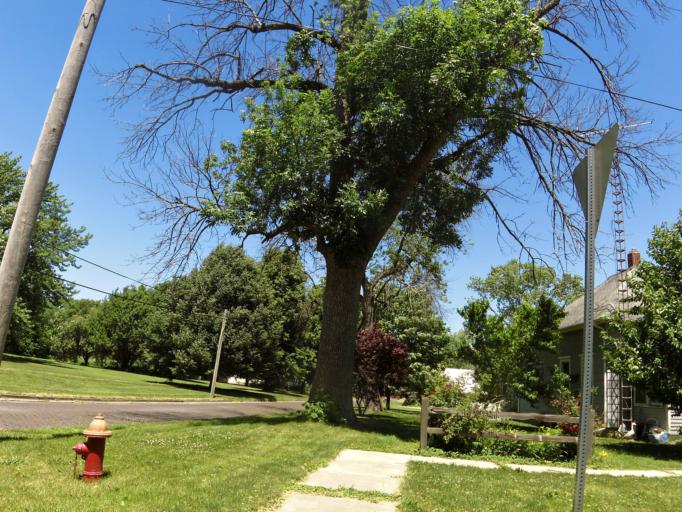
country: US
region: Illinois
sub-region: Iroquois County
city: Gilman
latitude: 40.7711
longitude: -87.9926
